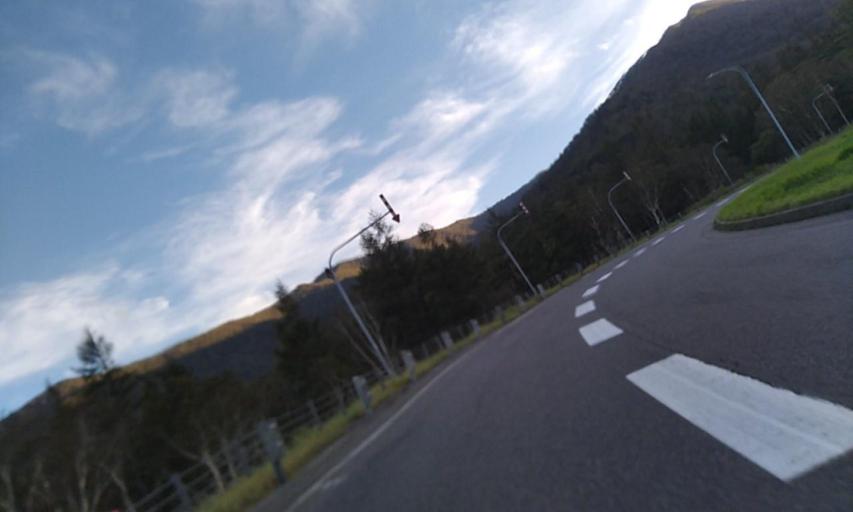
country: JP
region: Hokkaido
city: Otofuke
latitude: 42.9572
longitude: 142.7948
